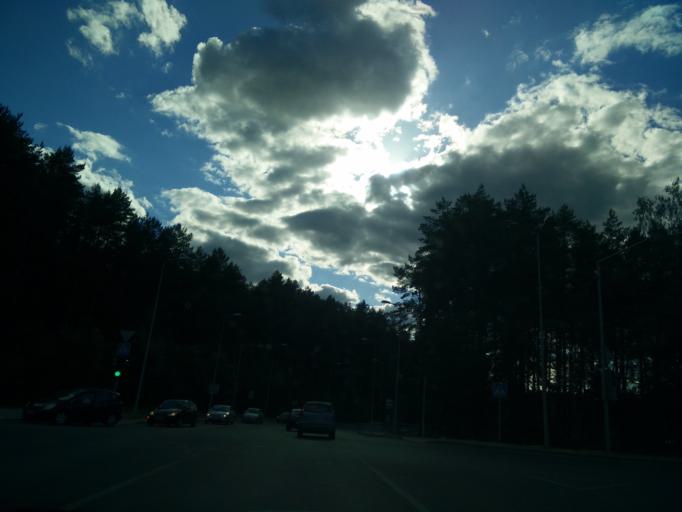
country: LT
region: Vilnius County
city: Lazdynai
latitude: 54.6702
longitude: 25.1986
